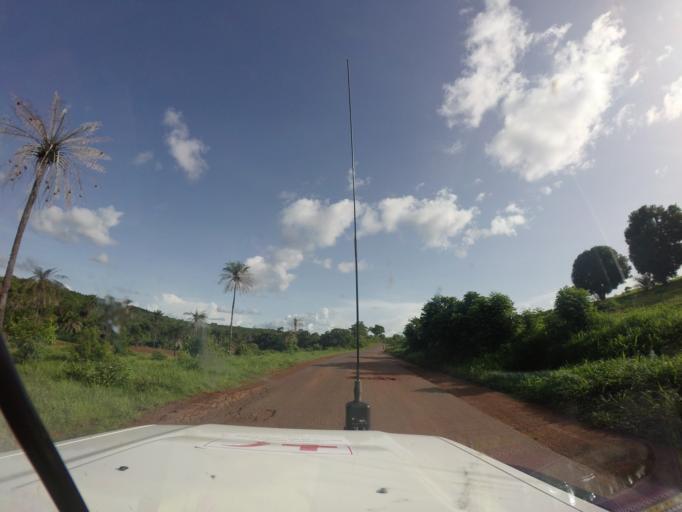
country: GN
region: Kindia
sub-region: Kindia
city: Kindia
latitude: 10.0907
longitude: -12.5716
